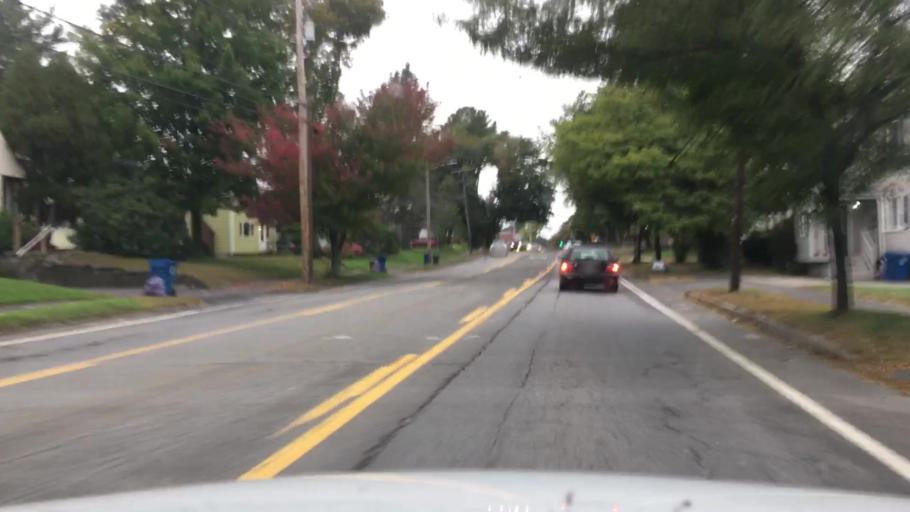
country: US
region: Maine
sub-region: Cumberland County
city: South Portland Gardens
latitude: 43.6721
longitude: -70.3110
